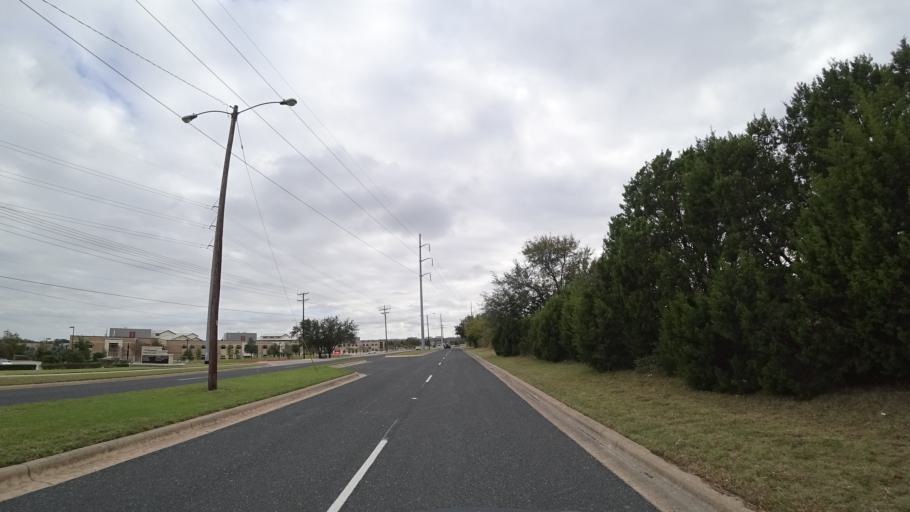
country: US
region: Texas
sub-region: Williamson County
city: Round Rock
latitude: 30.5109
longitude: -97.7014
